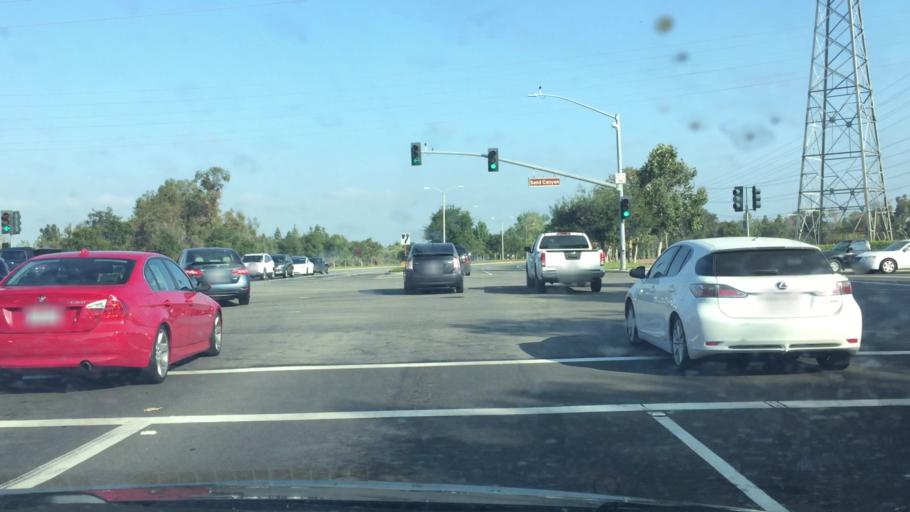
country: US
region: California
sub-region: Orange County
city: Irvine
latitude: 33.6645
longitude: -117.7708
